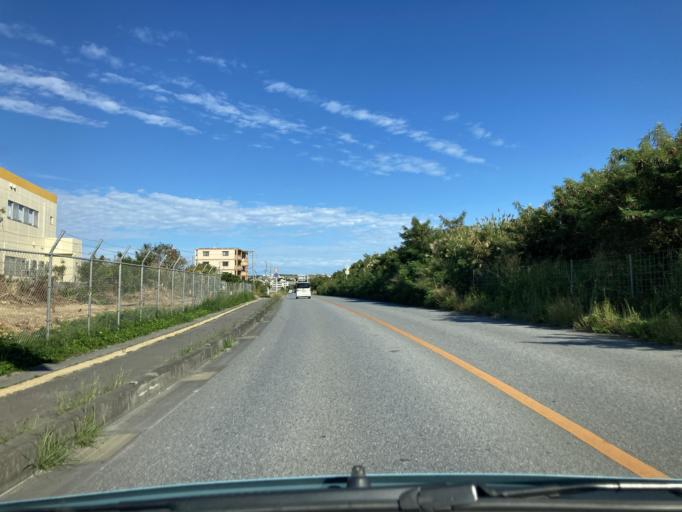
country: JP
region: Okinawa
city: Okinawa
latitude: 26.3716
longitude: 127.7463
